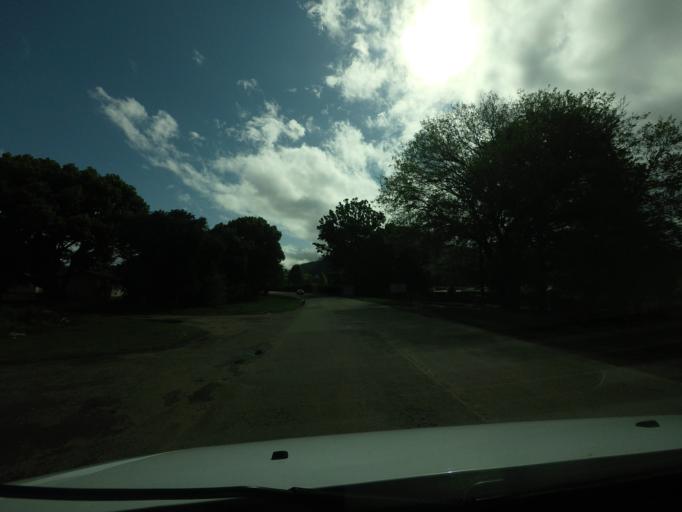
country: ZA
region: Mpumalanga
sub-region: Ehlanzeni District
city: Graksop
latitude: -25.0914
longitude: 30.7757
